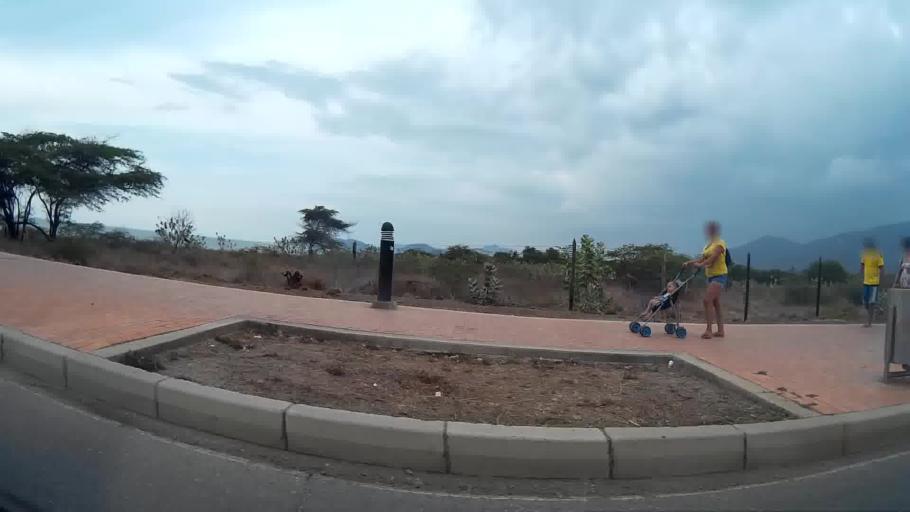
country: CO
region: Magdalena
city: Santa Marta
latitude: 11.1279
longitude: -74.2299
